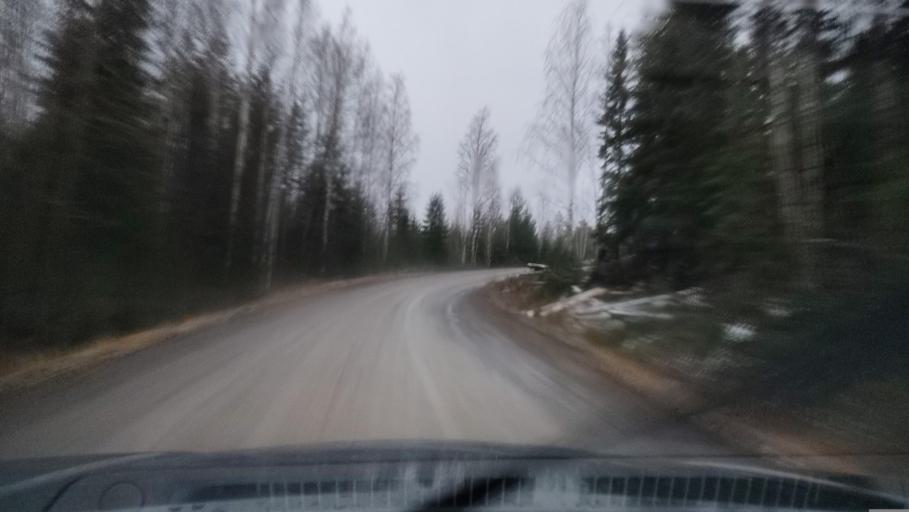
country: FI
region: Southern Ostrobothnia
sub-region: Suupohja
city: Karijoki
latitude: 62.1293
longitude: 21.6127
